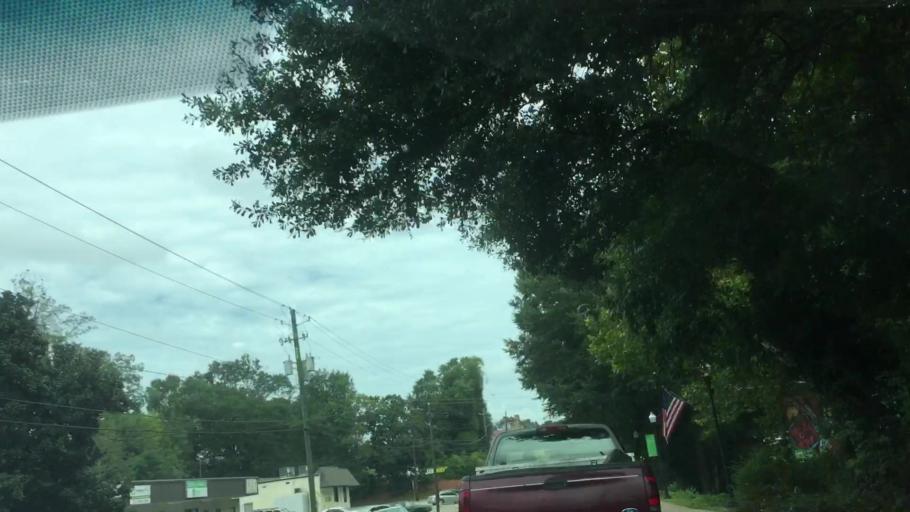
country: US
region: Alabama
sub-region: Hale County
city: Greensboro
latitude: 32.7018
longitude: -87.5954
